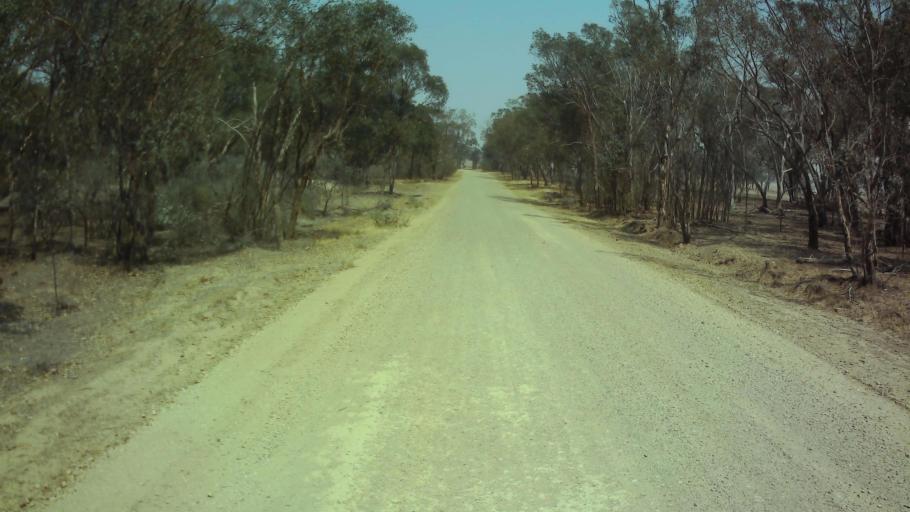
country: AU
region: New South Wales
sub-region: Weddin
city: Grenfell
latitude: -33.6451
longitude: 148.2630
